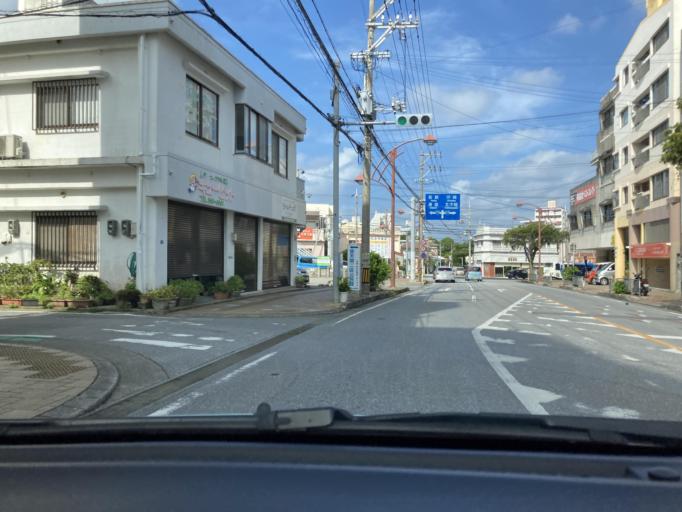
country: JP
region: Okinawa
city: Chatan
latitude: 26.2895
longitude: 127.7785
